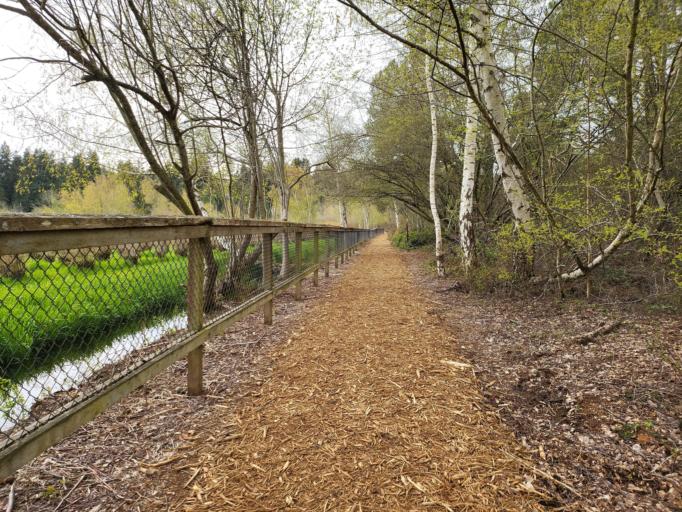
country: US
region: Washington
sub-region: King County
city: Bellevue
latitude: 47.5929
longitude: -122.1897
